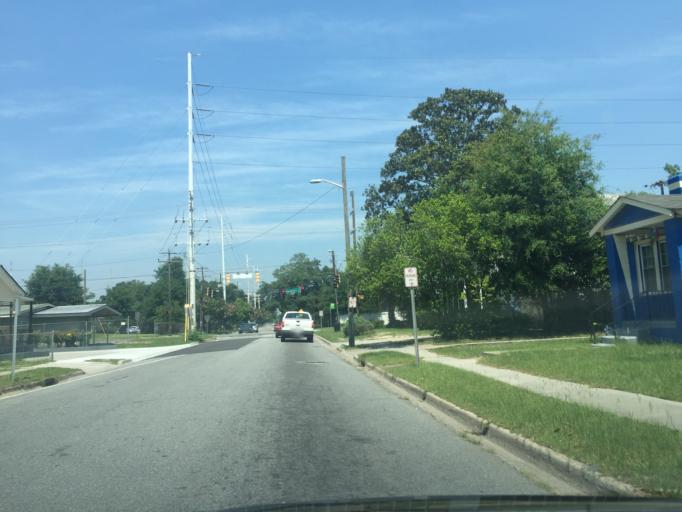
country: US
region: Georgia
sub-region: Chatham County
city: Savannah
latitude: 32.0468
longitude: -81.1079
